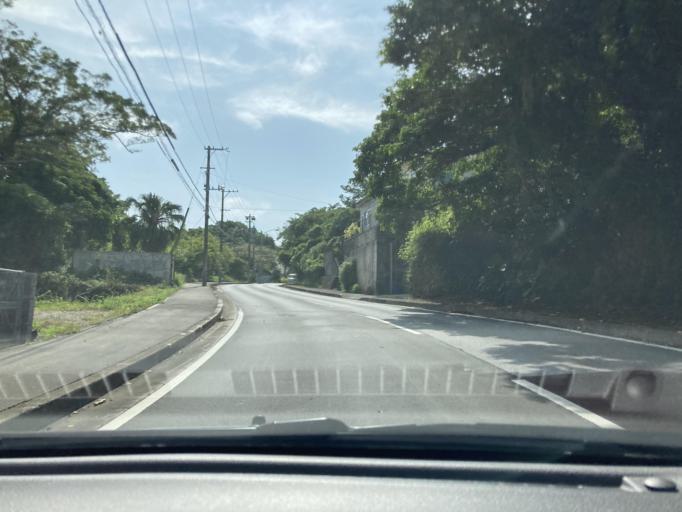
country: JP
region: Okinawa
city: Chatan
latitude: 26.2941
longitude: 127.7955
